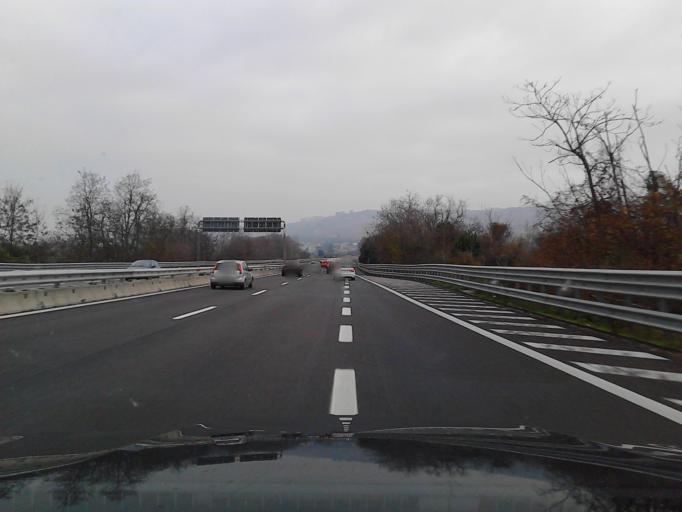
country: IT
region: Abruzzo
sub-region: Provincia di Teramo
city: Alba Adriatica
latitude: 42.8352
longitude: 13.9047
